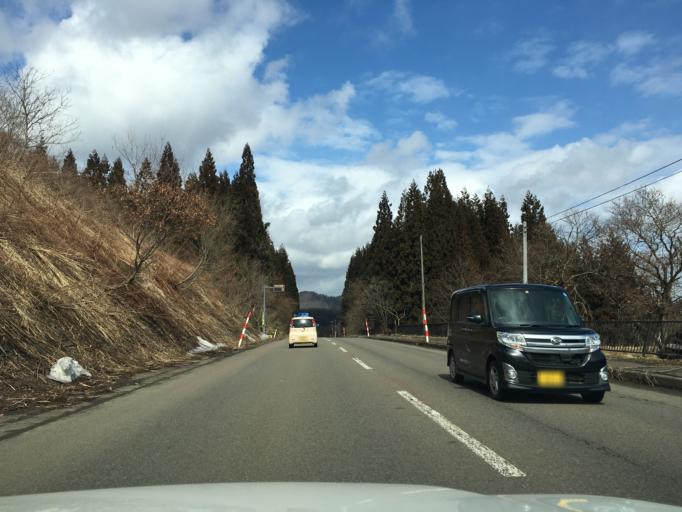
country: JP
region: Akita
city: Takanosu
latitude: 40.0207
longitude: 140.2750
